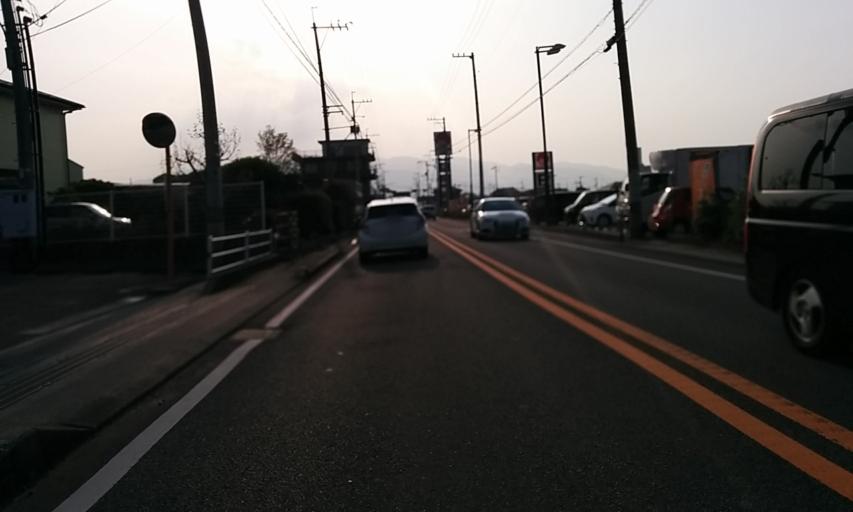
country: JP
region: Ehime
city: Saijo
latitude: 33.8958
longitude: 133.1265
